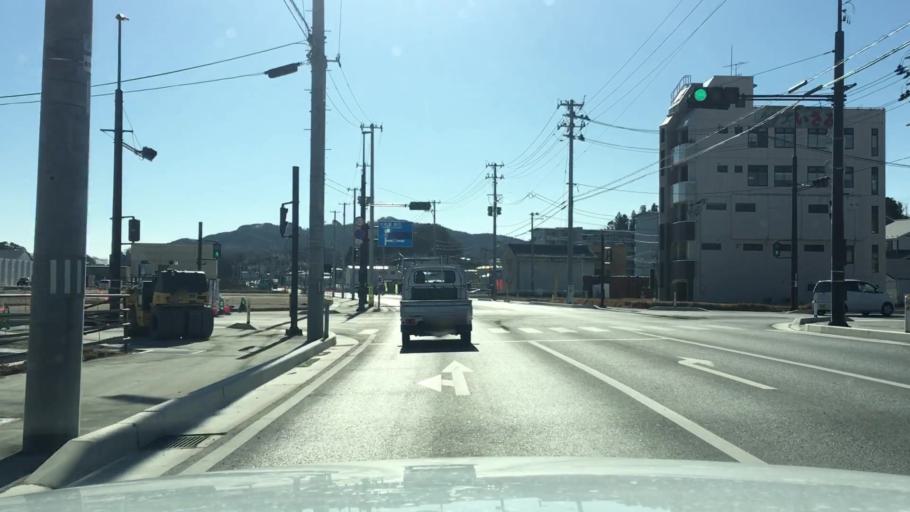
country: JP
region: Iwate
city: Yamada
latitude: 39.4660
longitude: 141.9524
